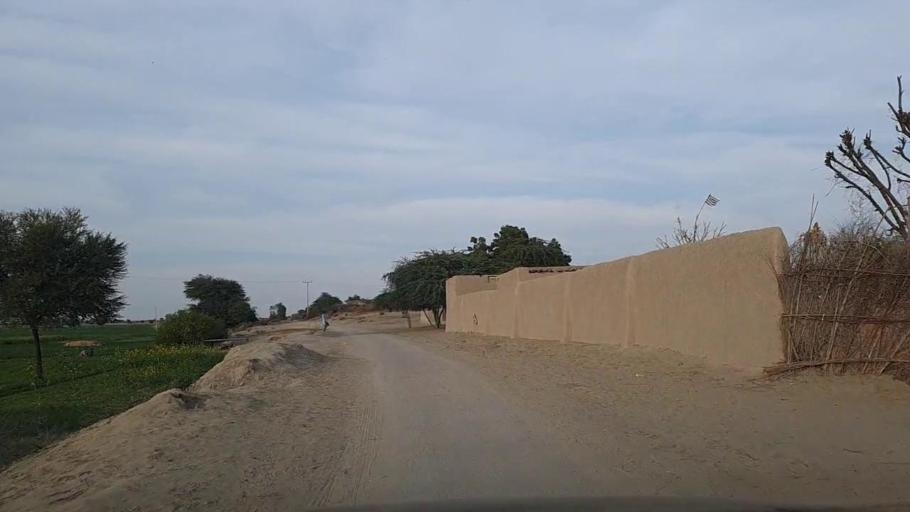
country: PK
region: Sindh
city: Jam Sahib
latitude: 26.4643
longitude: 68.5737
